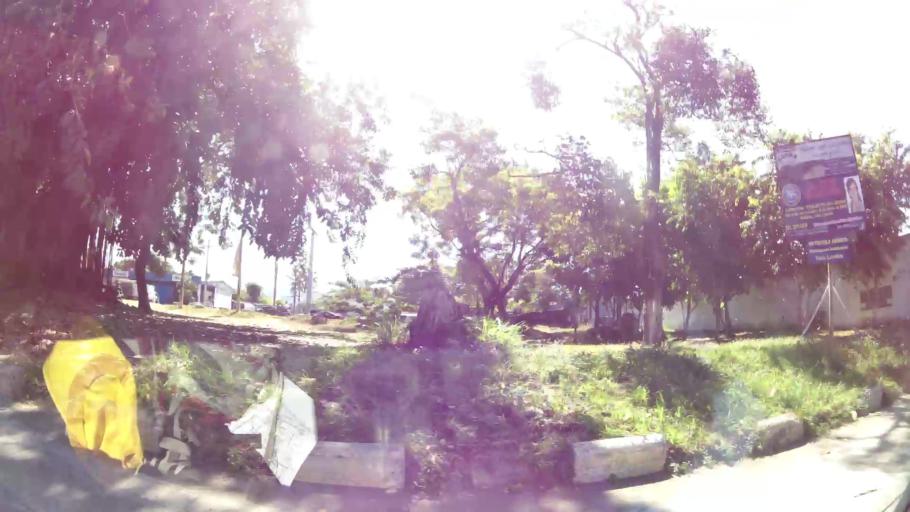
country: SV
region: La Libertad
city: Santa Tecla
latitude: 13.7242
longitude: -89.3704
